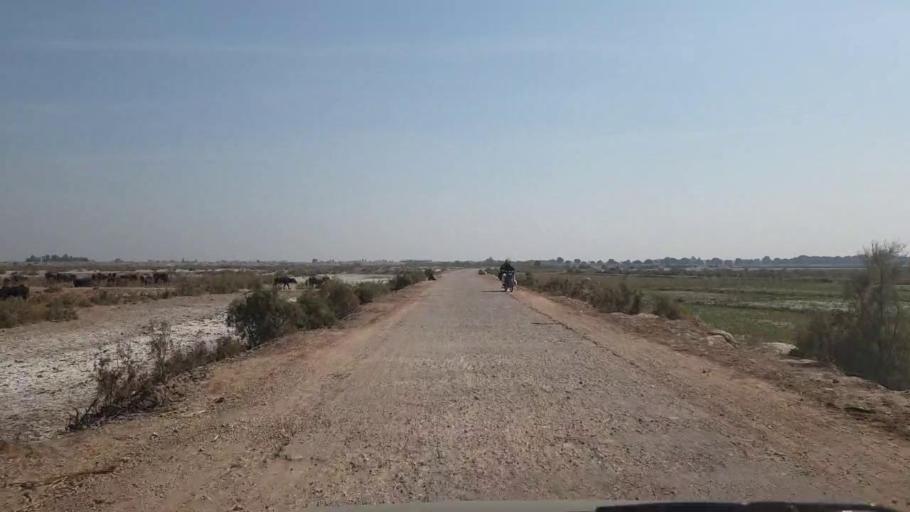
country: PK
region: Sindh
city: Chambar
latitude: 25.3846
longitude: 68.8005
